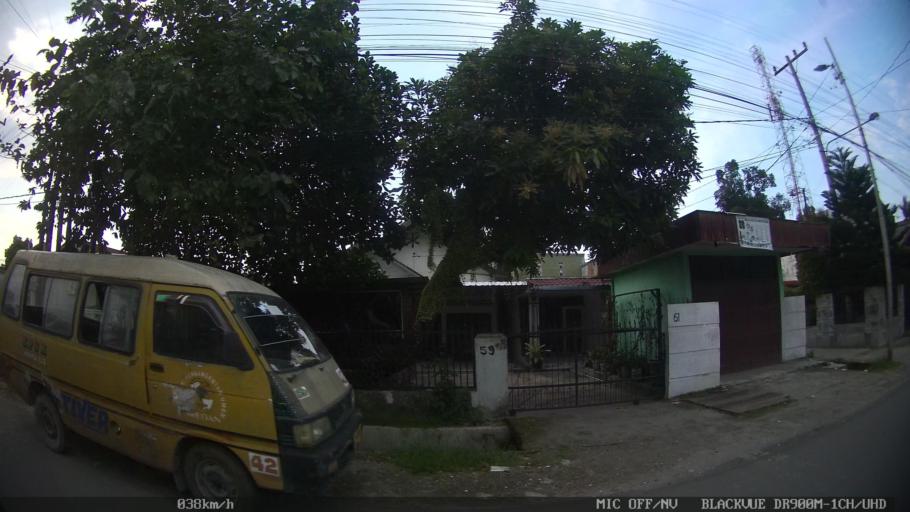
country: ID
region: North Sumatra
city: Medan
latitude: 3.6098
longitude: 98.6892
